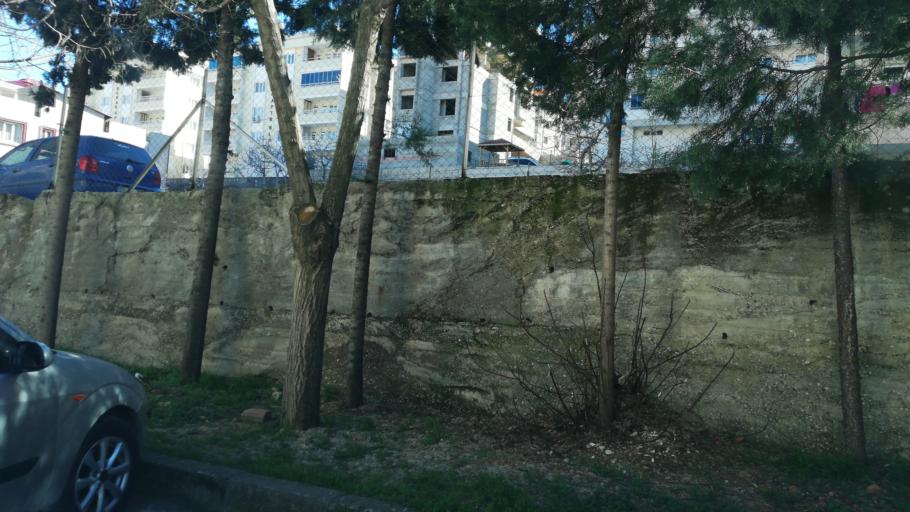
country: TR
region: Kahramanmaras
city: Kahramanmaras
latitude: 37.5836
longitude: 36.9092
